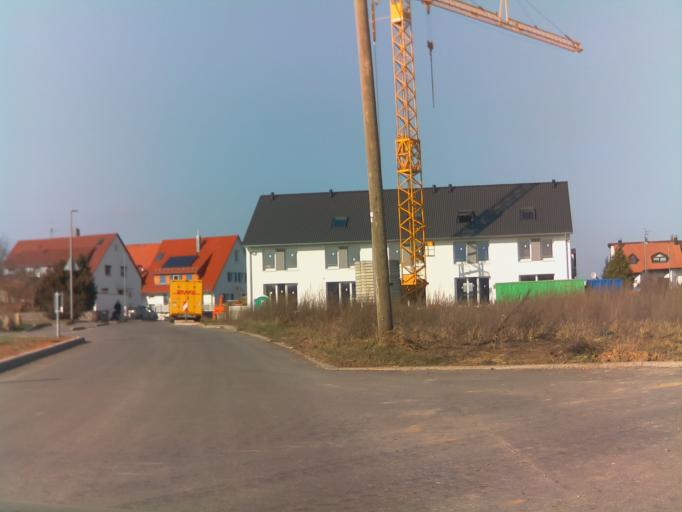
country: DE
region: Baden-Wuerttemberg
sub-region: Regierungsbezirk Stuttgart
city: Ehningen
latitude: 48.6854
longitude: 8.9568
